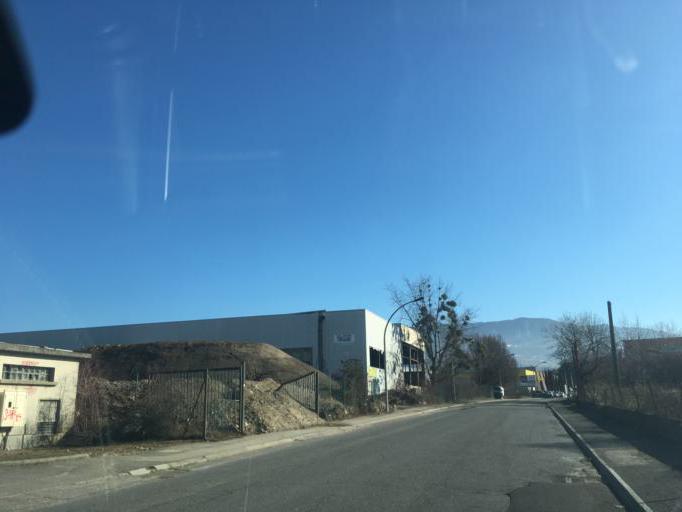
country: FR
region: Rhone-Alpes
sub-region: Departement de la Haute-Savoie
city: Ville-la-Grand
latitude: 46.1984
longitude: 6.2605
